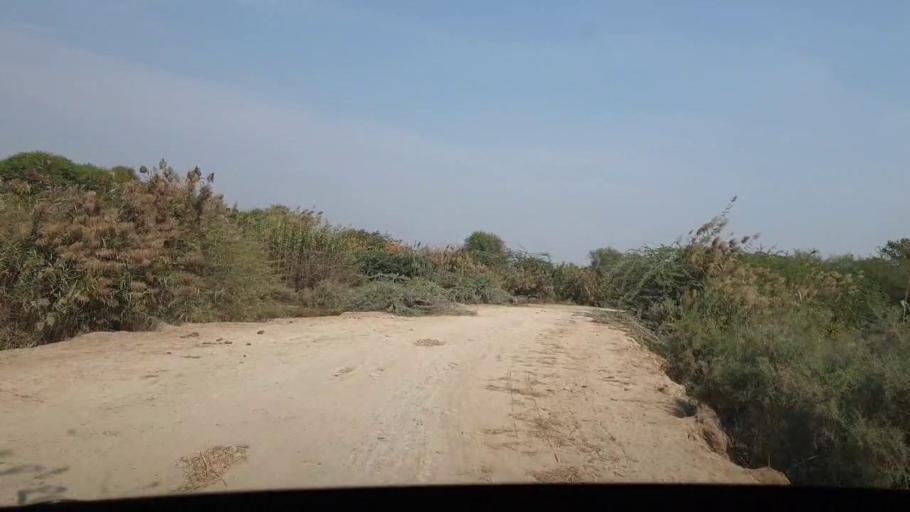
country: PK
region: Sindh
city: Chuhar Jamali
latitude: 24.2686
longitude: 67.9564
